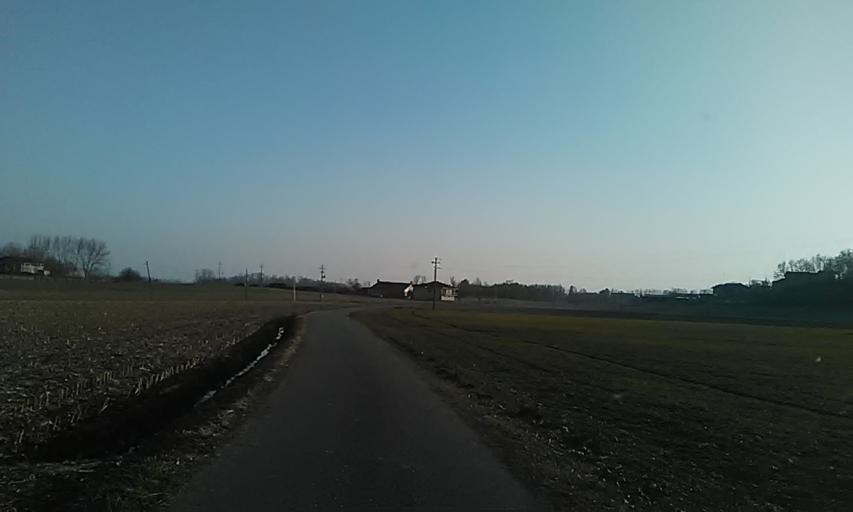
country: IT
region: Piedmont
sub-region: Provincia di Biella
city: Dorzano
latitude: 45.4134
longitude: 8.1173
